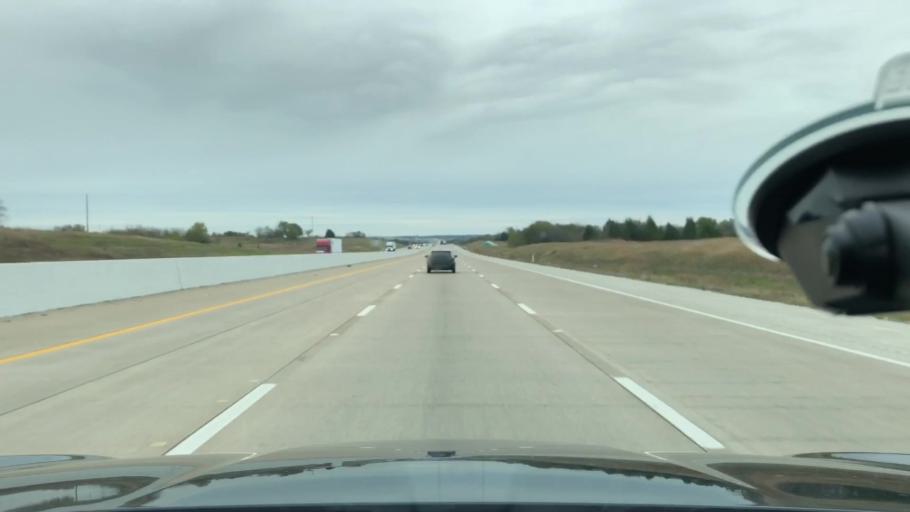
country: US
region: Texas
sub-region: Ellis County
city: Italy
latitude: 32.2084
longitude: -96.8932
